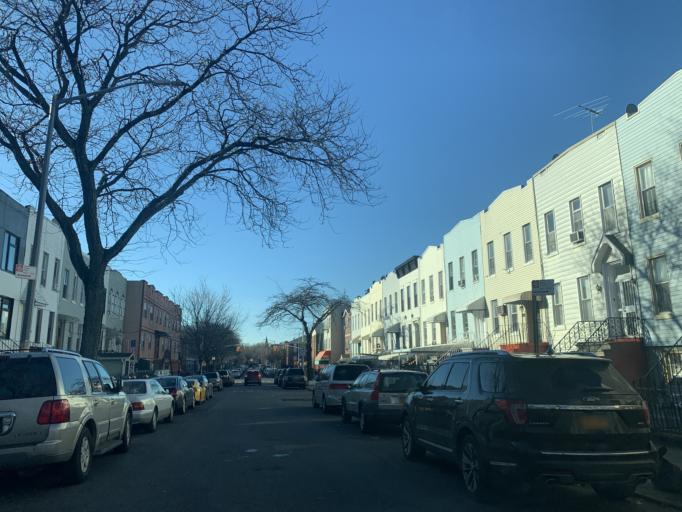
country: US
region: New York
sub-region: Kings County
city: East New York
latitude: 40.6952
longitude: -73.9141
